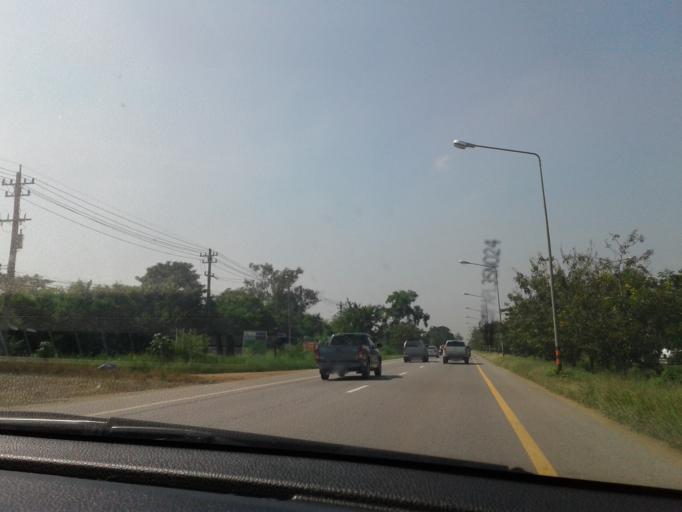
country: TH
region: Ratchaburi
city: Bang Phae
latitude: 13.7647
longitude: 99.9293
